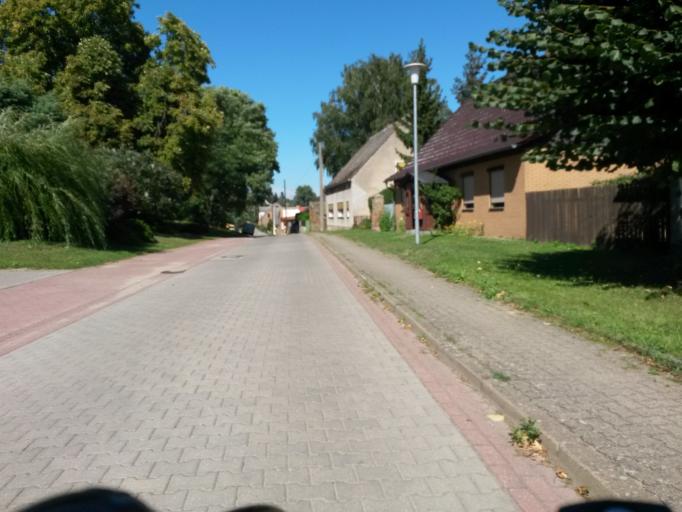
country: DE
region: Brandenburg
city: Schoneberg
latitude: 52.9251
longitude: 14.1213
